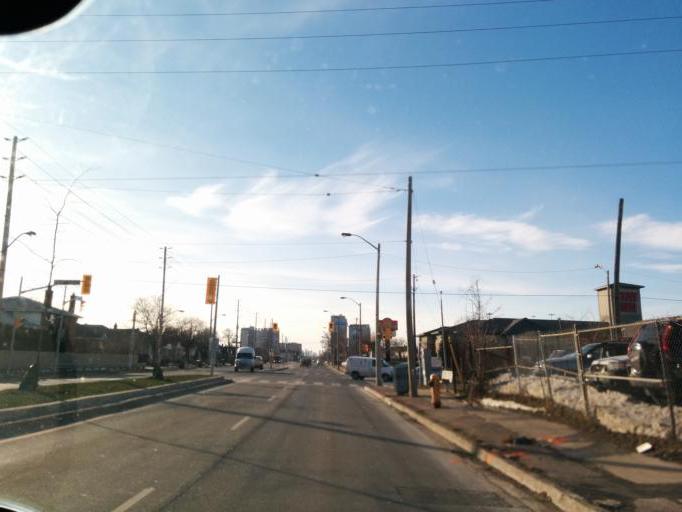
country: CA
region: Ontario
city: Etobicoke
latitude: 43.6121
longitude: -79.5431
